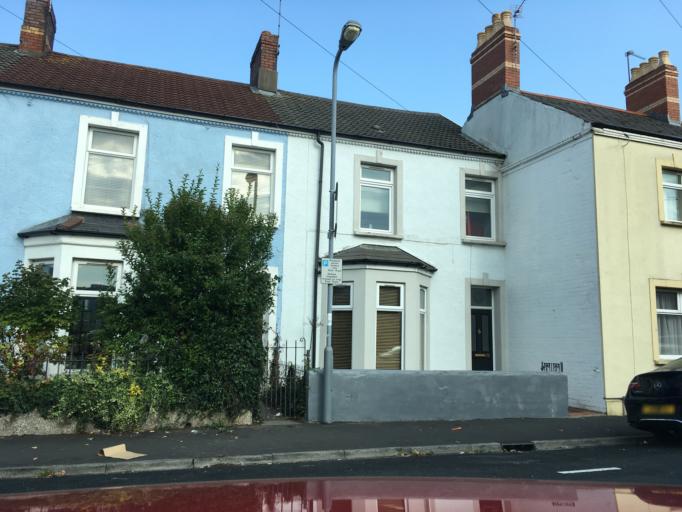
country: GB
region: Wales
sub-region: Cardiff
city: Cardiff
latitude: 51.4890
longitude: -3.1579
